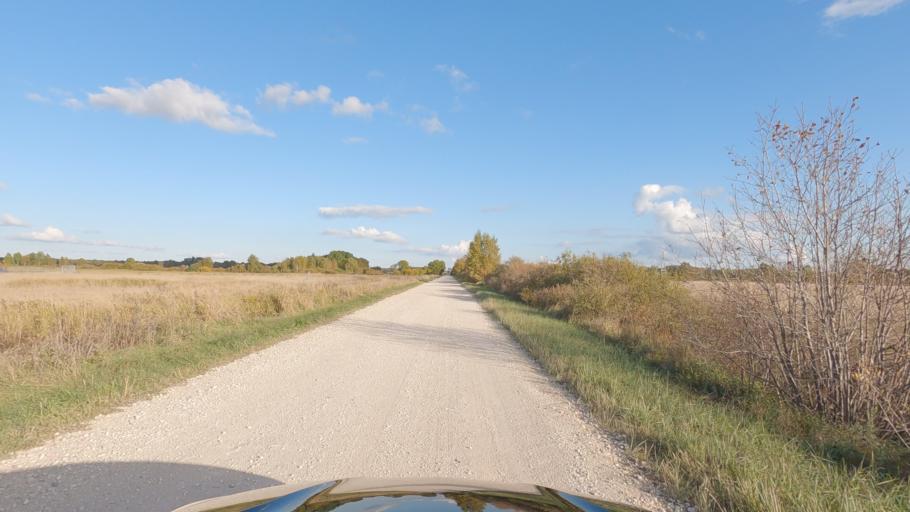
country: EE
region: Harju
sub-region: Saku vald
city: Saku
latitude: 59.2892
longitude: 24.6822
